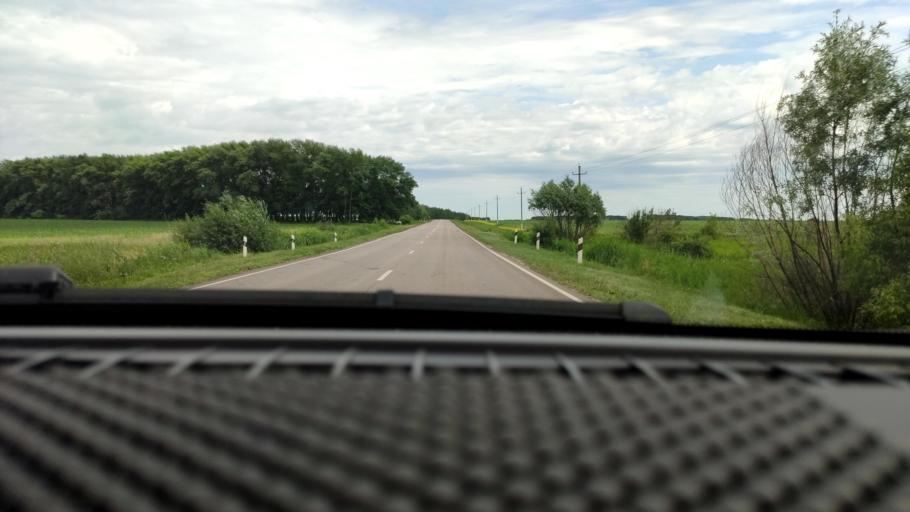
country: RU
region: Voronezj
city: Panino
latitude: 51.6567
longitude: 39.9987
